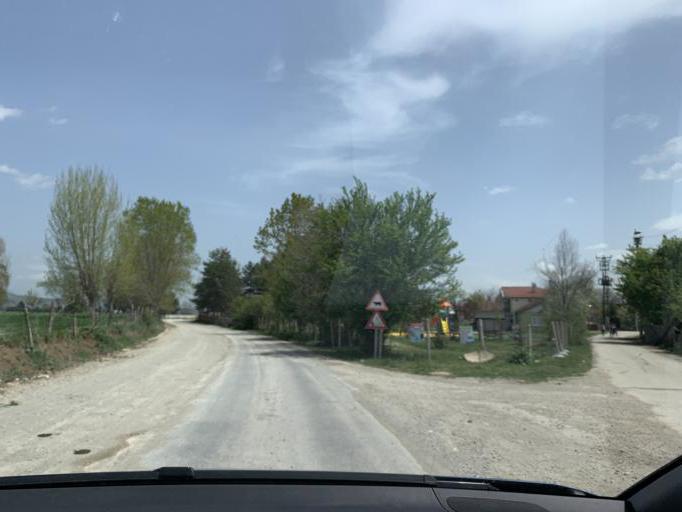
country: TR
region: Bolu
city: Bolu
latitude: 40.7428
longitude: 31.6543
